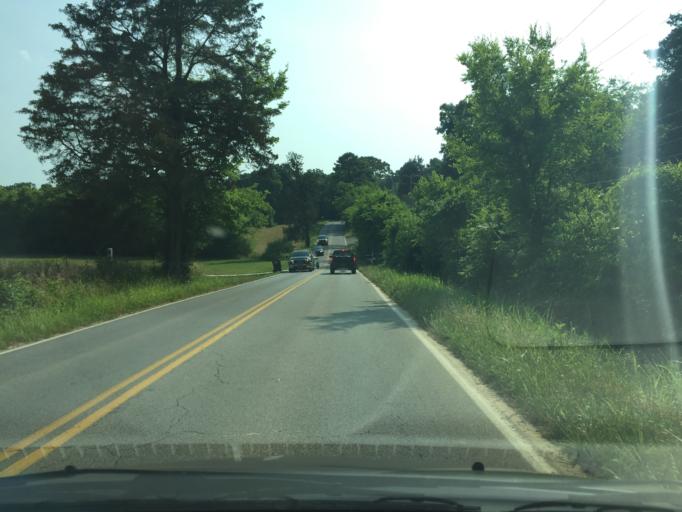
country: US
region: Tennessee
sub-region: Hamilton County
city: Middle Valley
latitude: 35.1741
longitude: -85.1623
